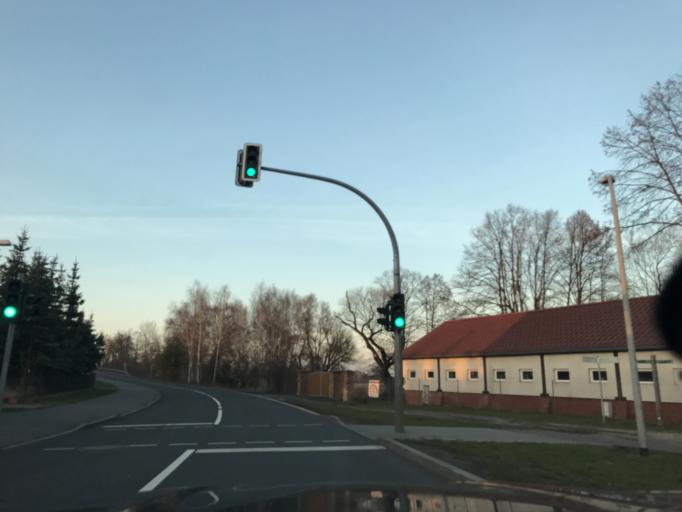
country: DE
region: Brandenburg
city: Brandenburg an der Havel
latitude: 52.4891
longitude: 12.4622
